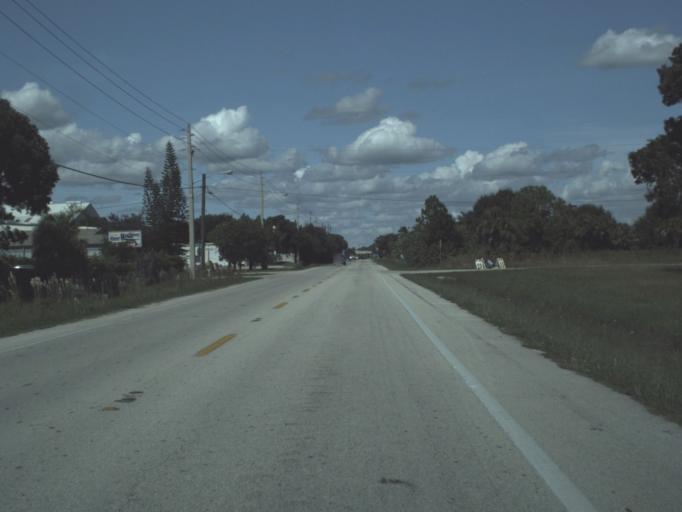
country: US
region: Florida
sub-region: Lee County
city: Fort Myers
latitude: 26.6148
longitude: -81.8518
